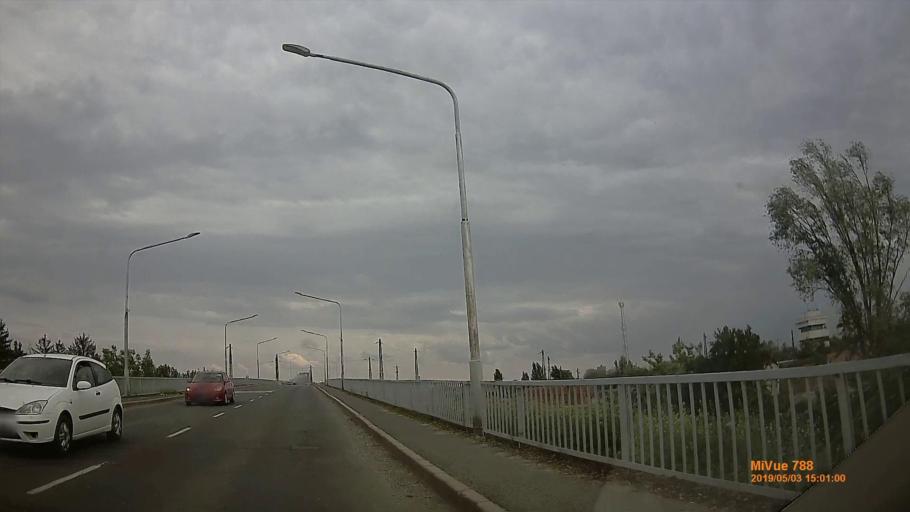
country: HU
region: Jasz-Nagykun-Szolnok
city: Szolnok
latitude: 47.1869
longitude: 20.1805
